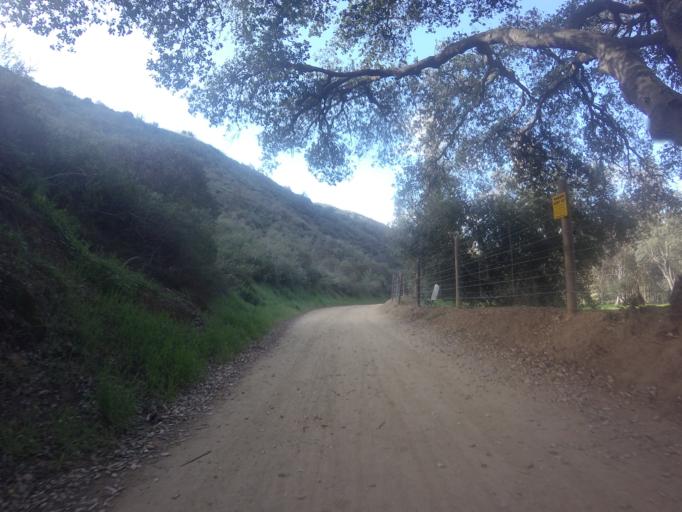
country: US
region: California
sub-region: Orange County
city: Foothill Ranch
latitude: 33.7783
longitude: -117.6737
